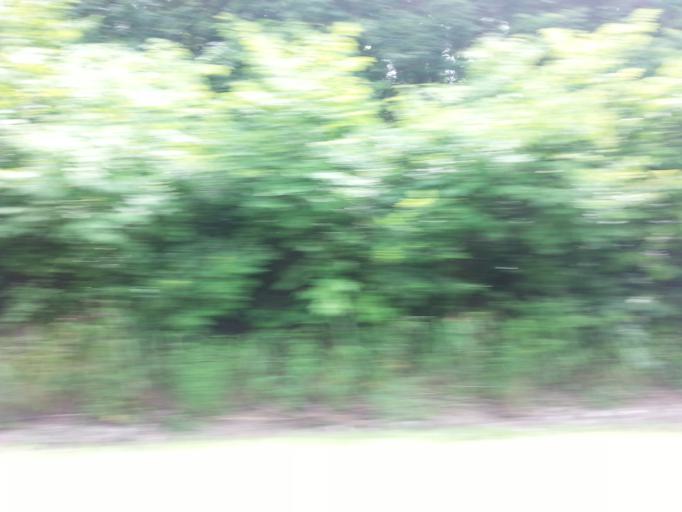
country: US
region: Tennessee
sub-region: Putnam County
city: Algood
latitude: 36.1436
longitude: -85.3676
